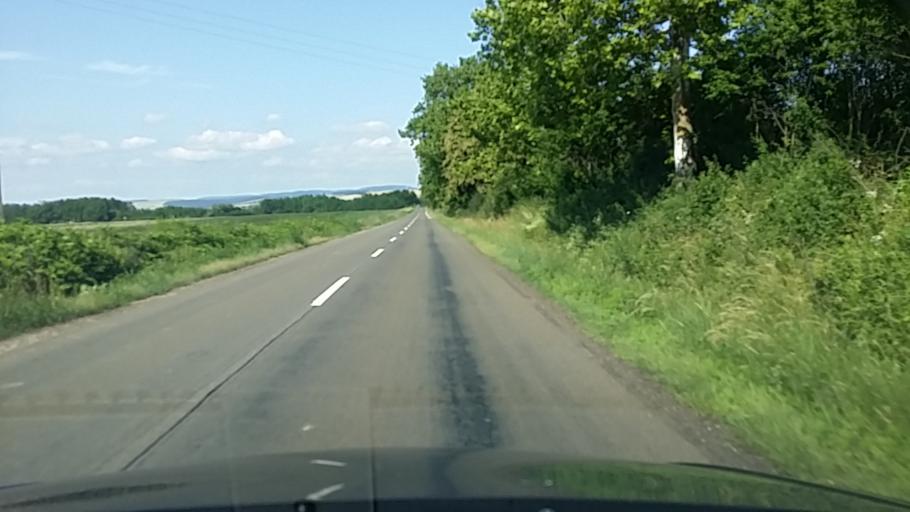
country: SK
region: Nitriansky
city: Sahy
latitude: 48.0518
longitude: 18.9247
